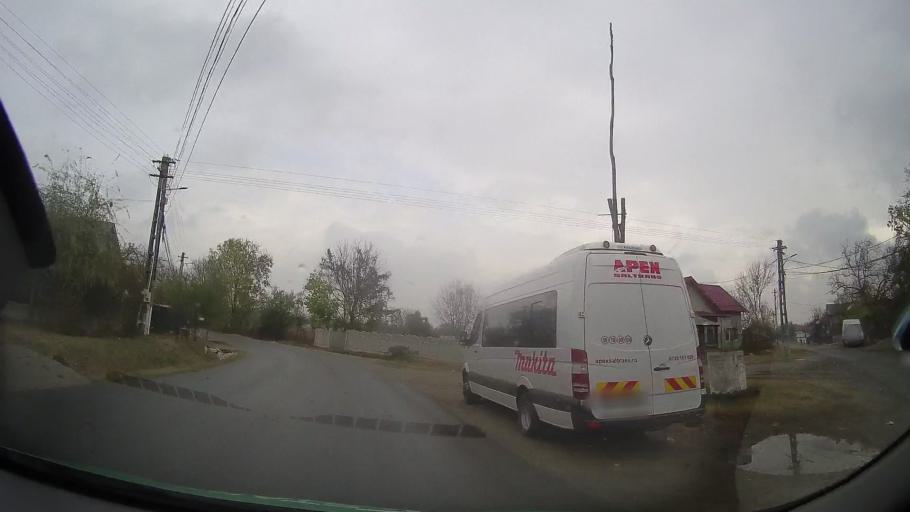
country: RO
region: Prahova
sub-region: Comuna Gherghita
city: Gherghita
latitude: 44.7990
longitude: 26.2855
